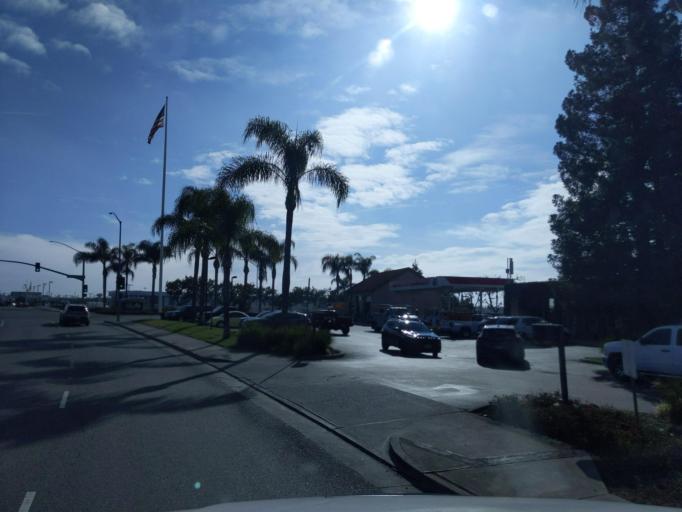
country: US
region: California
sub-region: San Joaquin County
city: Morada
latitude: 38.0207
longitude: -121.2717
